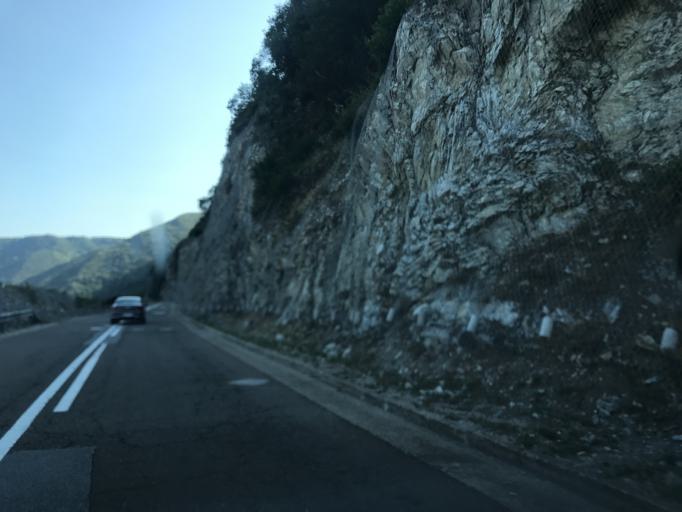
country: RO
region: Caras-Severin
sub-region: Comuna Berzasca
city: Berzasca
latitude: 44.5874
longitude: 22.0222
